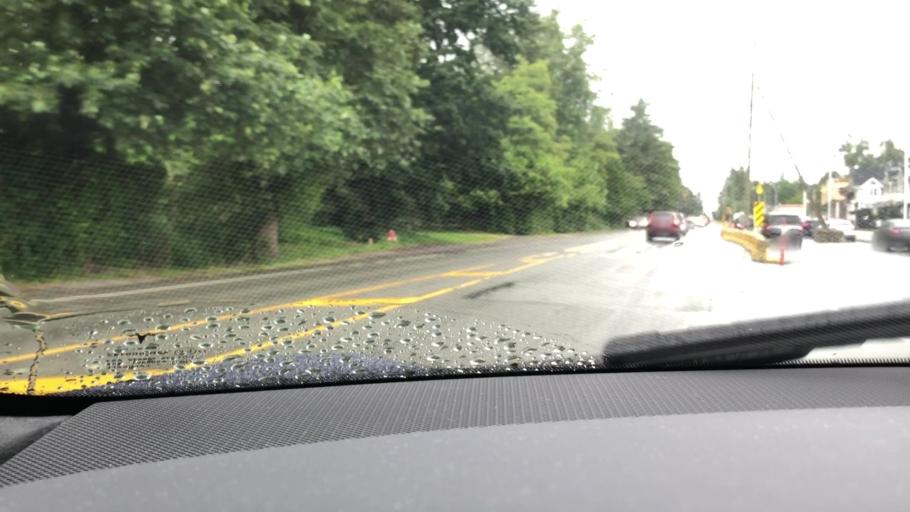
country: CA
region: British Columbia
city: Walnut Grove
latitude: 49.1327
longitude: -122.6455
